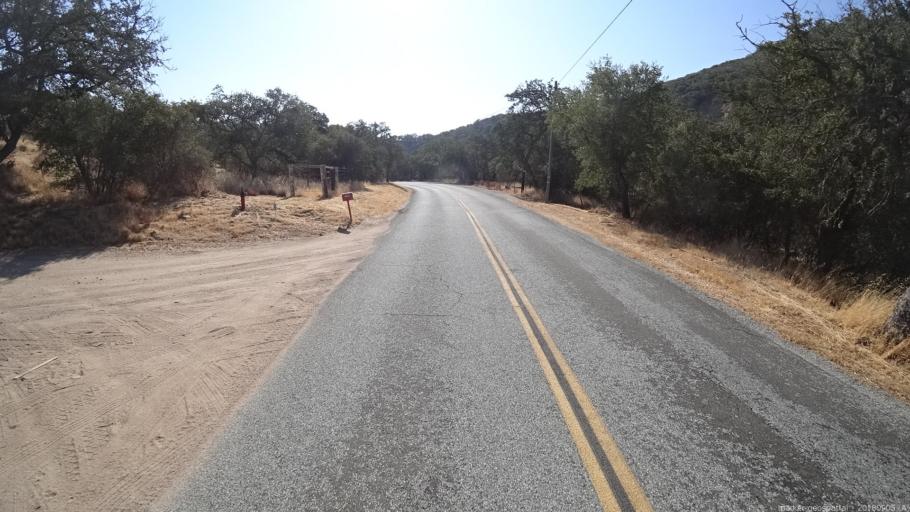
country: US
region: California
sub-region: Monterey County
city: Soledad
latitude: 36.2700
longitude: -121.4436
